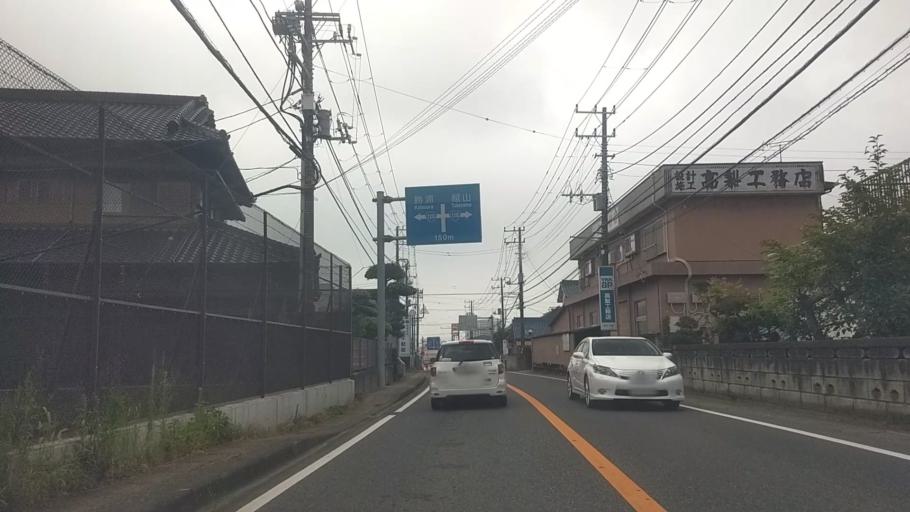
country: JP
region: Chiba
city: Kawaguchi
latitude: 35.1107
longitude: 140.0995
